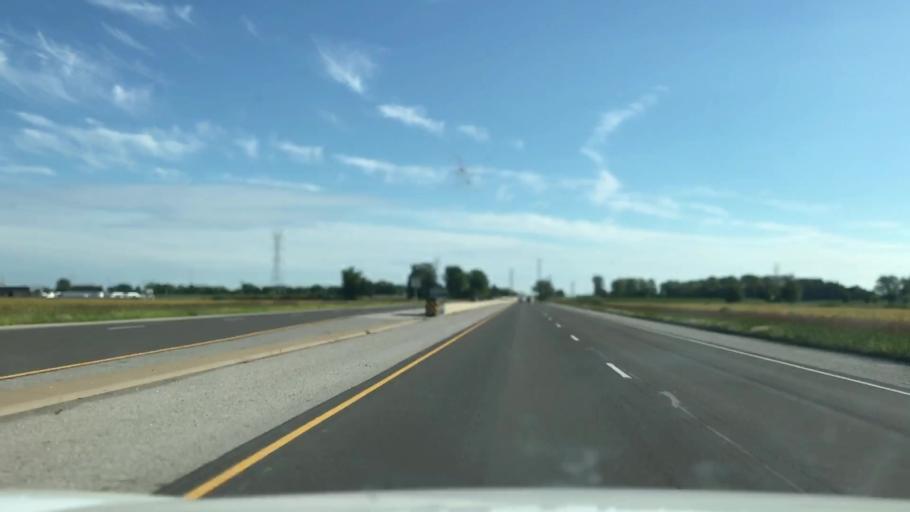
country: US
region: Illinois
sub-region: Madison County
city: Hartford
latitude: 38.8130
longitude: -90.0987
